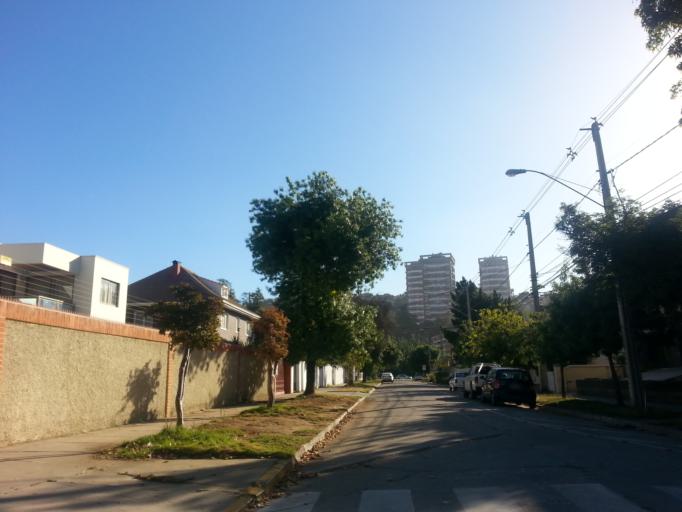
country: CL
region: Valparaiso
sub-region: Provincia de Valparaiso
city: Vina del Mar
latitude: -33.0283
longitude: -71.5333
